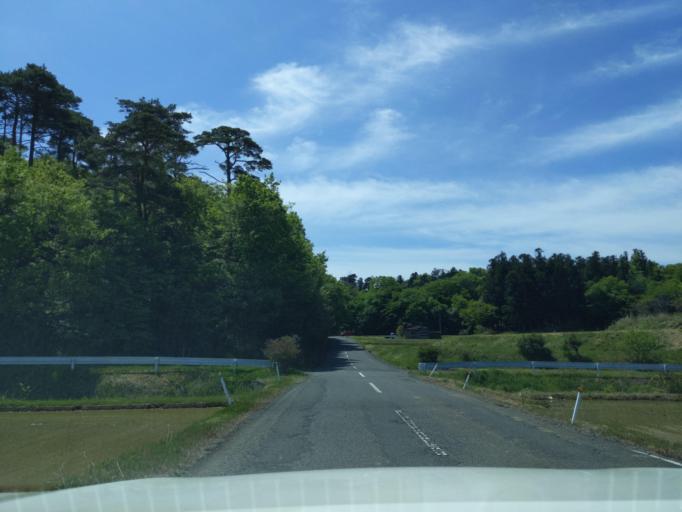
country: JP
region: Fukushima
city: Koriyama
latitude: 37.4184
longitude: 140.2969
